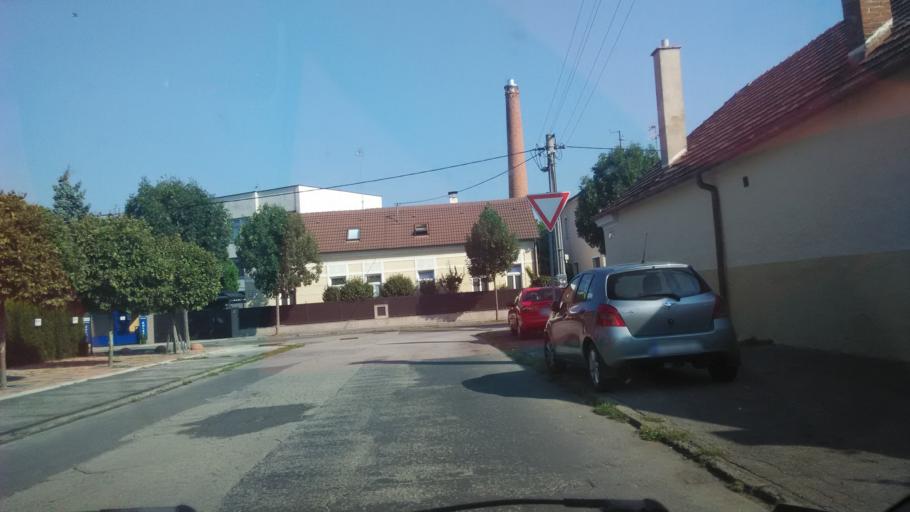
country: SK
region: Trnavsky
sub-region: Okres Trnava
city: Piestany
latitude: 48.5889
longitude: 17.8269
